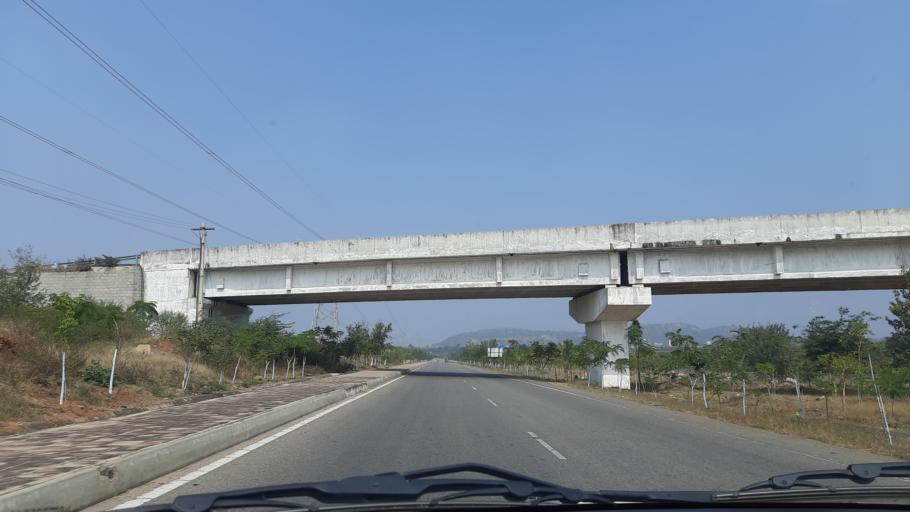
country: IN
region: Telangana
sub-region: Rangareddi
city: Lal Bahadur Nagar
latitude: 17.3075
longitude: 78.6551
